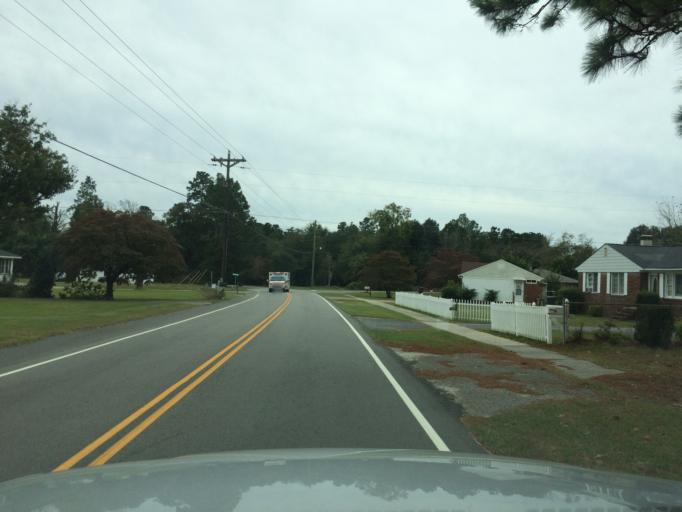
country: US
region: South Carolina
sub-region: Aiken County
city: New Ellenton
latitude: 33.4215
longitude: -81.6913
